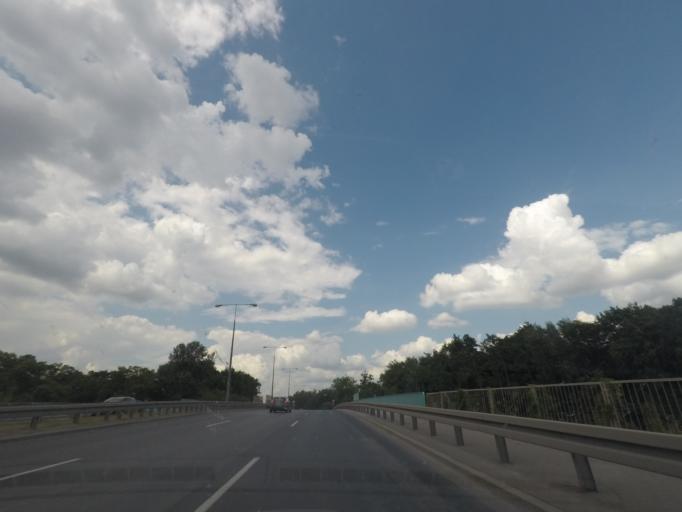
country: PL
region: Masovian Voivodeship
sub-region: Warszawa
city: Zoliborz
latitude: 52.2522
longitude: 20.9550
